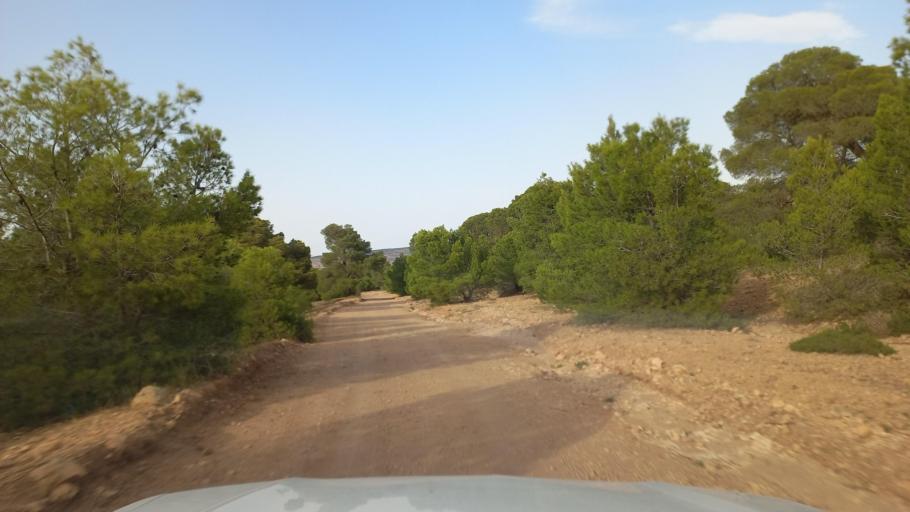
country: TN
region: Al Qasrayn
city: Kasserine
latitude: 35.3371
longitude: 8.8551
